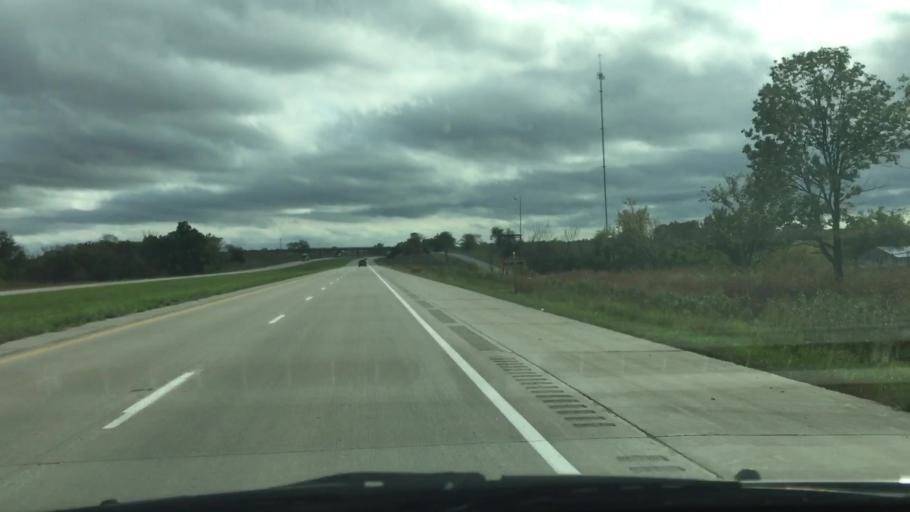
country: US
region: Iowa
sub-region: Decatur County
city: Leon
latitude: 40.7637
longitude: -93.8370
